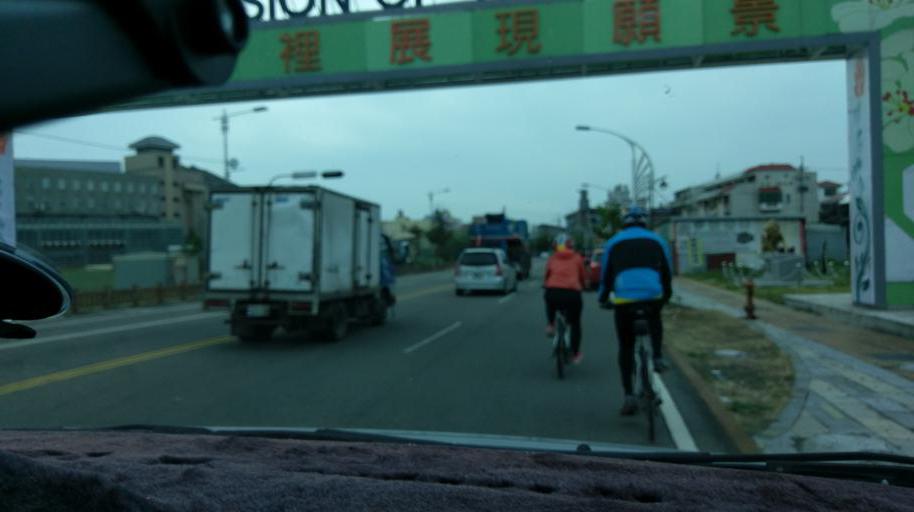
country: TW
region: Taiwan
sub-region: Miaoli
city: Miaoli
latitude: 24.4507
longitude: 120.6569
